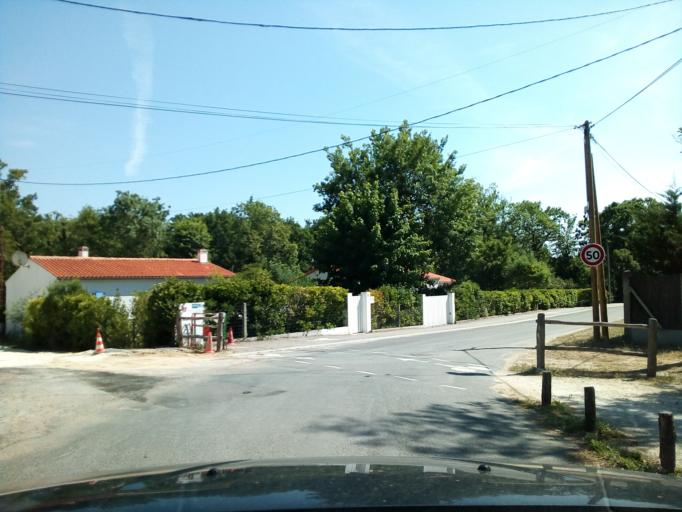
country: FR
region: Poitou-Charentes
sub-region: Departement de la Charente-Maritime
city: Boyard-Ville
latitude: 45.9809
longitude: -1.2940
